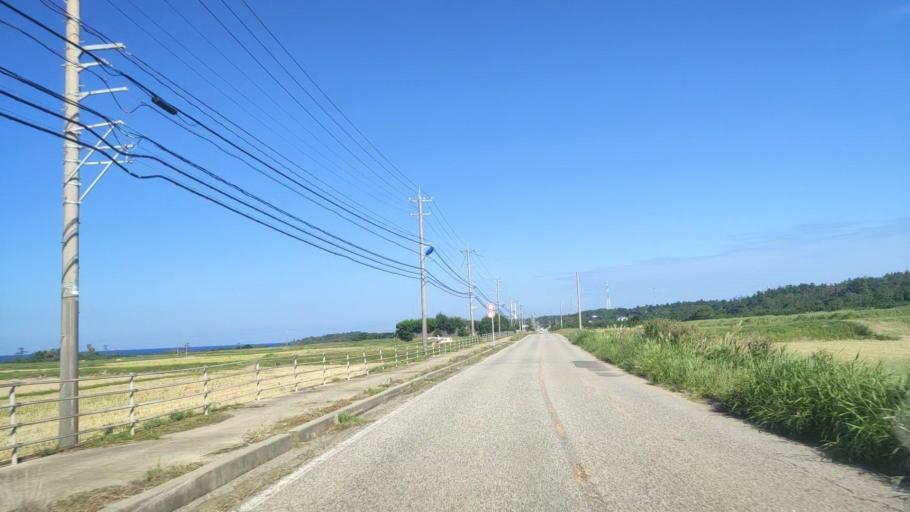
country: JP
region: Ishikawa
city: Hakui
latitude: 37.0400
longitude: 136.7419
